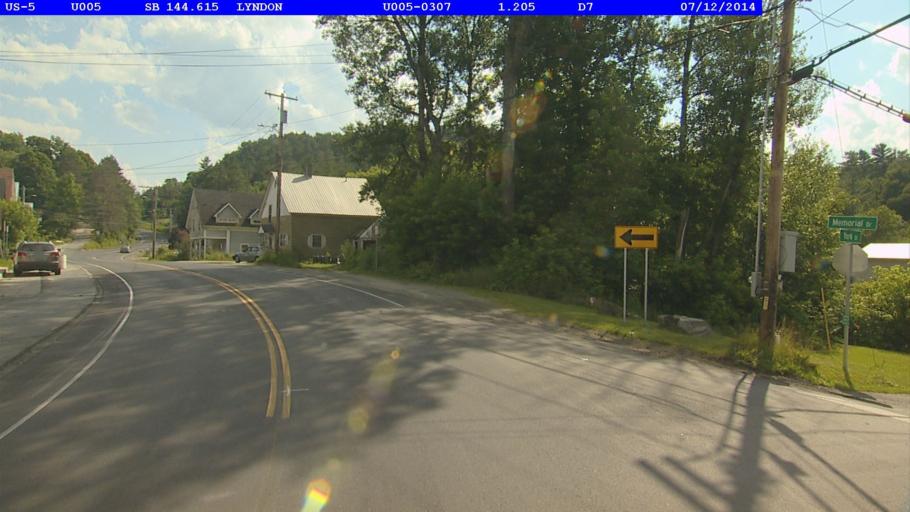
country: US
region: Vermont
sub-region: Caledonia County
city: Lyndon
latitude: 44.5141
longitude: -72.0108
